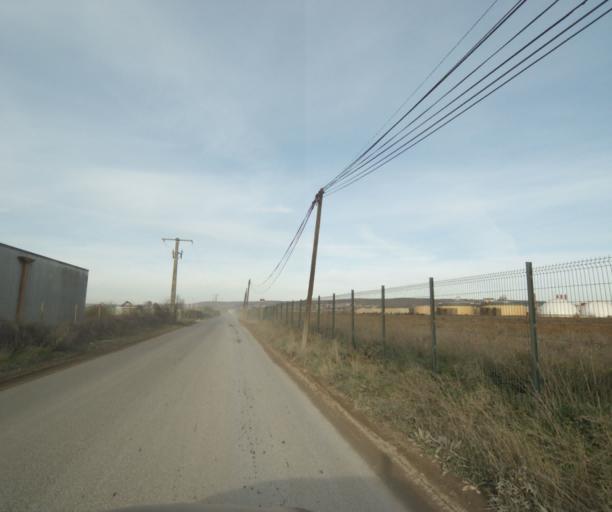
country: FR
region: Ile-de-France
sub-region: Departement des Yvelines
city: Medan
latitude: 48.9501
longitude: 2.0116
